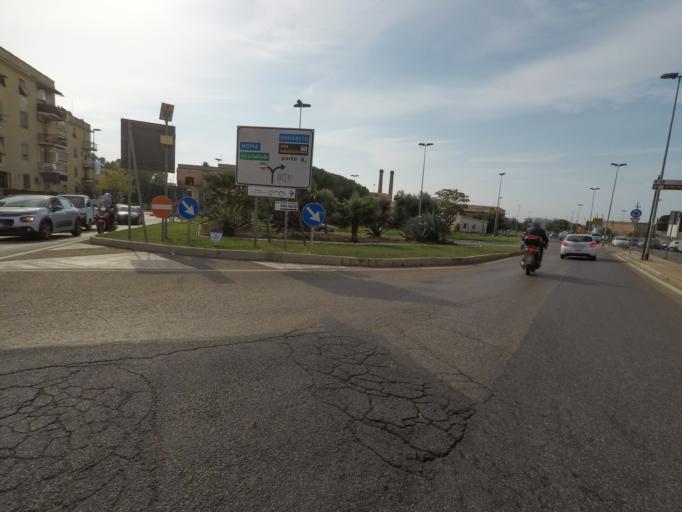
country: IT
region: Latium
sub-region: Citta metropolitana di Roma Capitale
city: Civitavecchia
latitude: 42.0993
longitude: 11.7997
